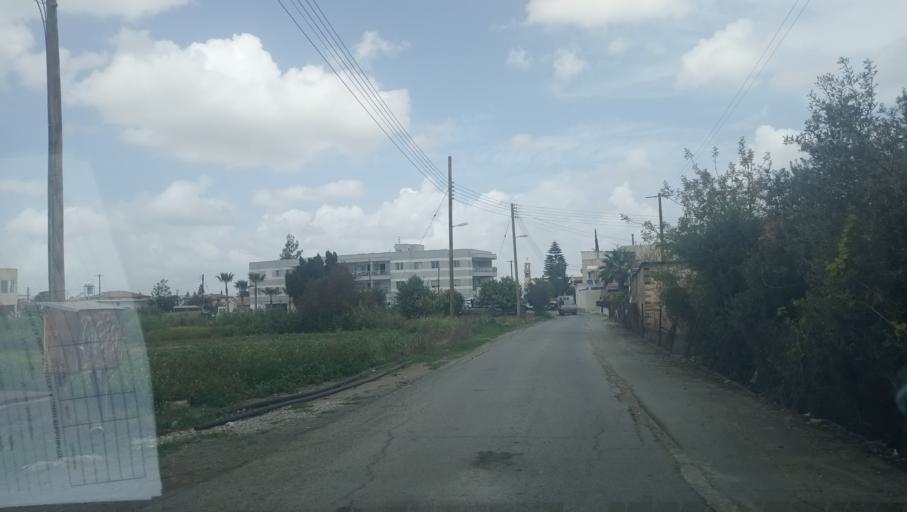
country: CY
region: Lefkosia
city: Pano Deftera
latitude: 35.0808
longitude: 33.2709
